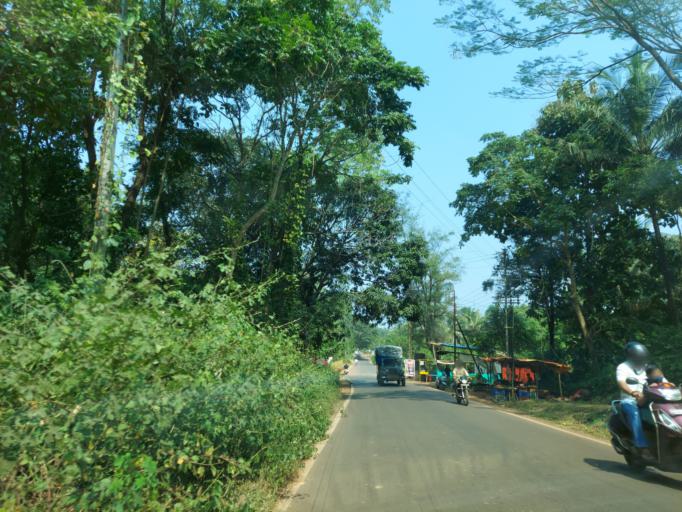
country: IN
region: Maharashtra
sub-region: Sindhudurg
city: Kudal
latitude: 15.9924
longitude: 73.6841
